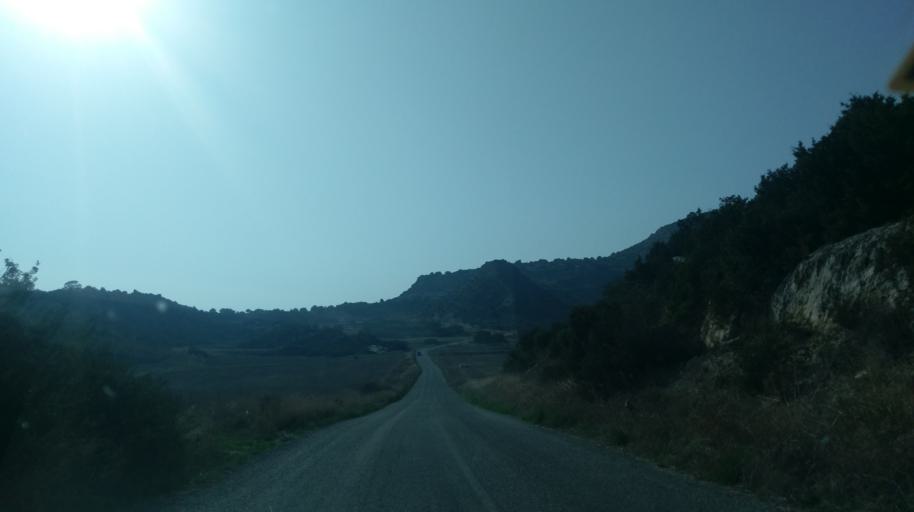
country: CY
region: Ammochostos
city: Rizokarpaso
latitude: 35.5260
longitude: 34.3259
